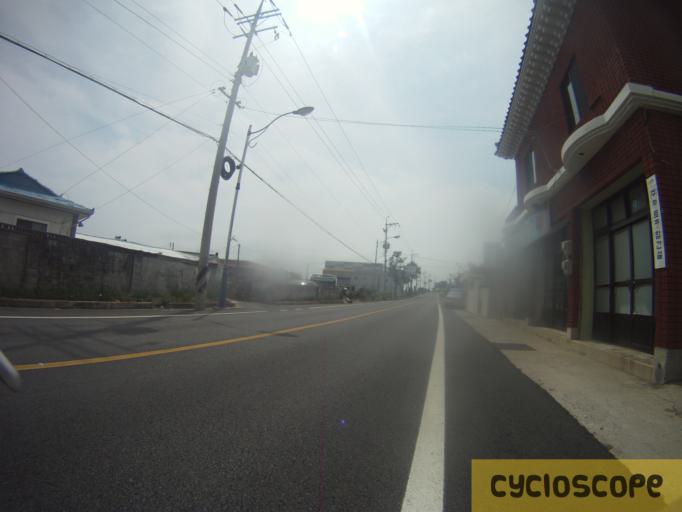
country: KR
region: Busan
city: Kijang
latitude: 35.2851
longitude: 129.2568
